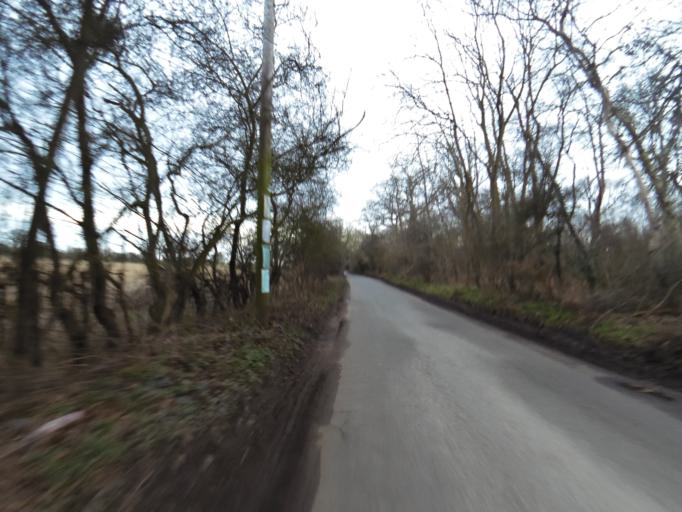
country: GB
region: England
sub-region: Suffolk
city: Ipswich
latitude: 52.0195
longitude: 1.1146
